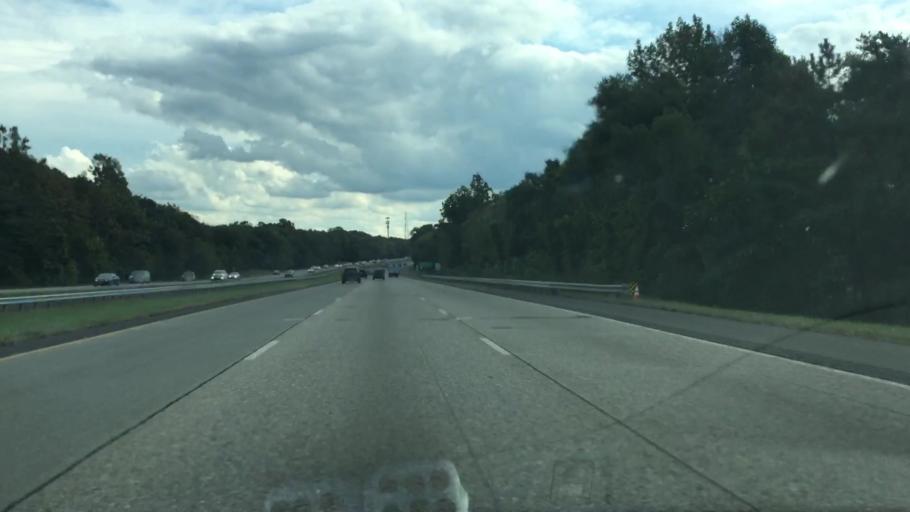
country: US
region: New Jersey
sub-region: Camden County
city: Blackwood
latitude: 39.8015
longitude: -75.0548
